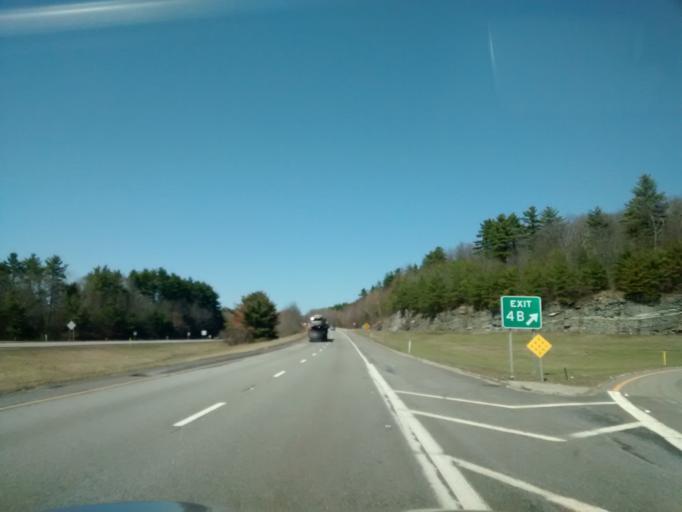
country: US
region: Massachusetts
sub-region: Worcester County
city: Oxford
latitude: 42.1177
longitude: -71.8549
